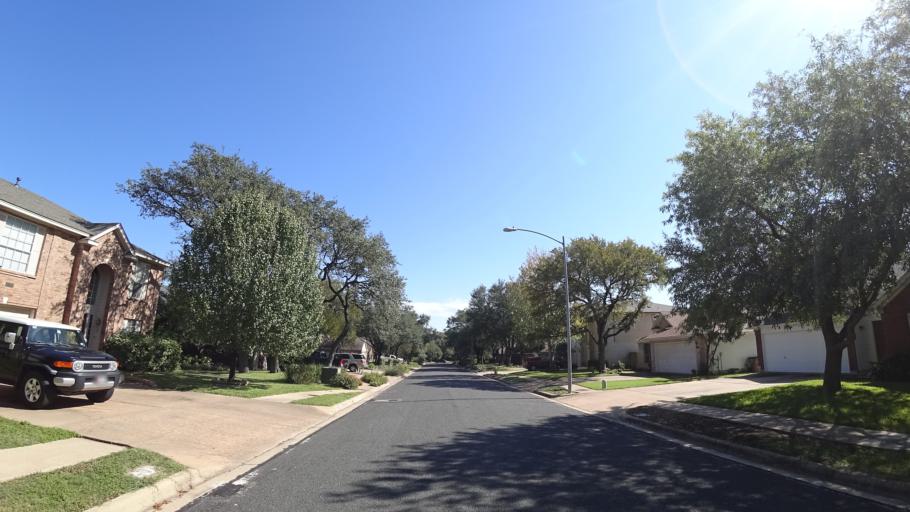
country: US
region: Texas
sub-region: Travis County
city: Shady Hollow
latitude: 30.2139
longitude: -97.8729
